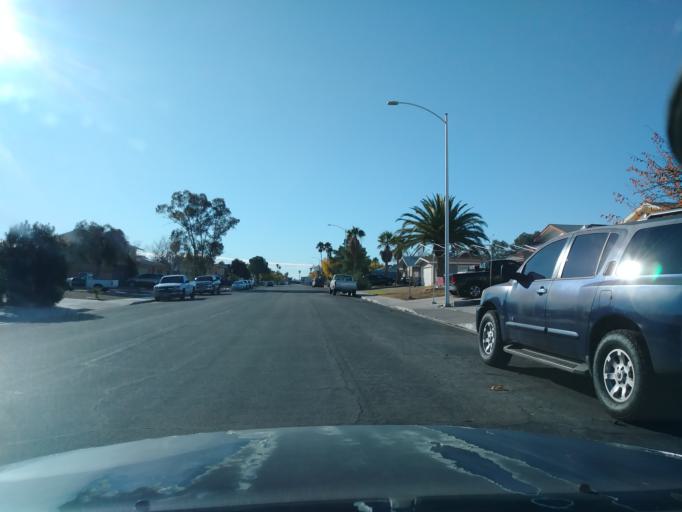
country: US
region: Nevada
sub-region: Clark County
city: Spring Valley
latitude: 36.1719
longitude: -115.2470
